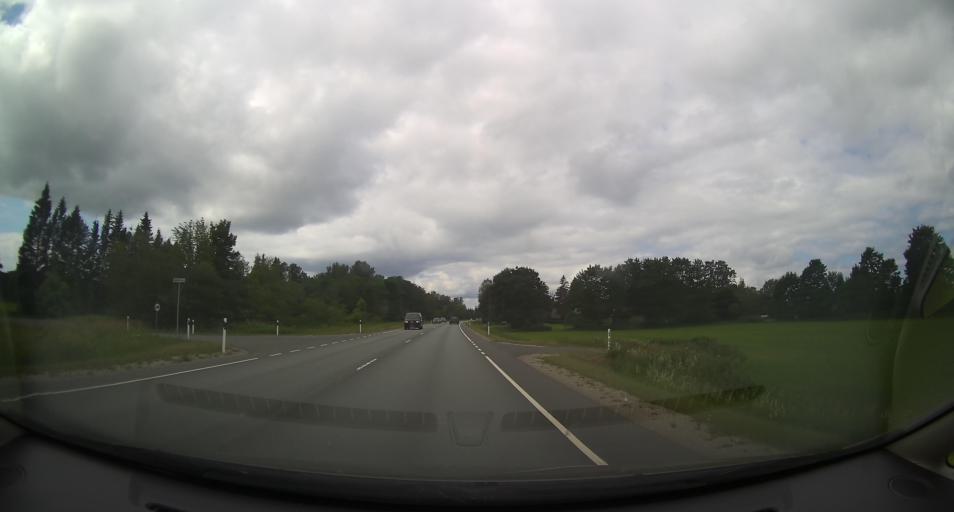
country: EE
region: Laeaene
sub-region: Lihula vald
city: Lihula
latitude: 58.6133
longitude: 23.5910
